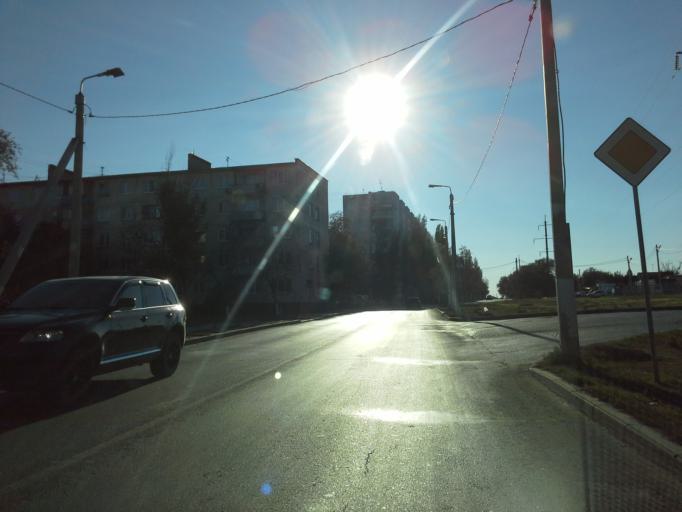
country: RU
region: Volgograd
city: Vodstroy
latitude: 48.8227
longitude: 44.6236
